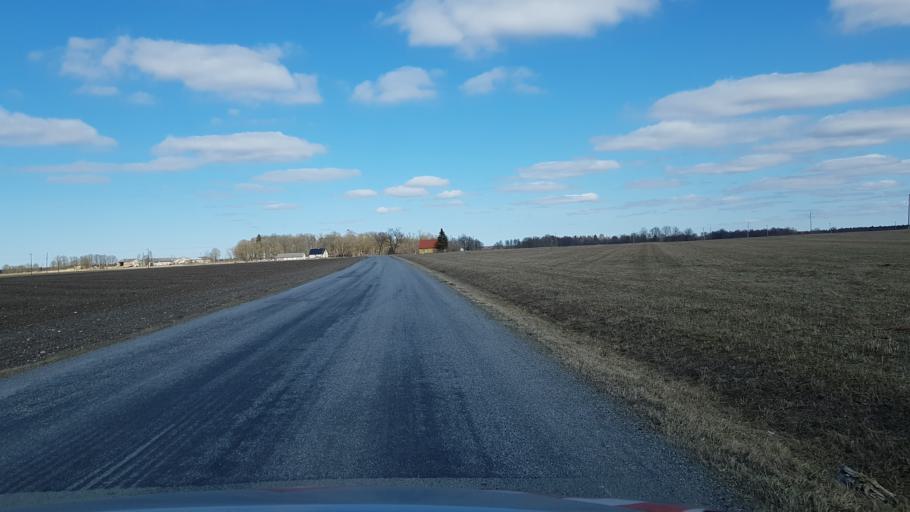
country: EE
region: Laeaene-Virumaa
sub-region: Tapa vald
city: Tapa
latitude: 59.2668
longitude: 25.8523
